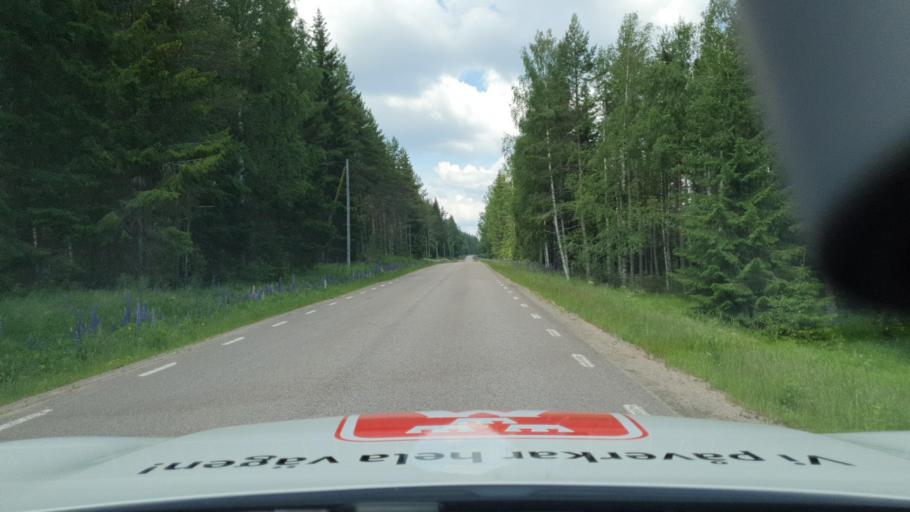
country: SE
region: Vaermland
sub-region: Torsby Kommun
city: Torsby
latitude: 60.4811
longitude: 12.8792
